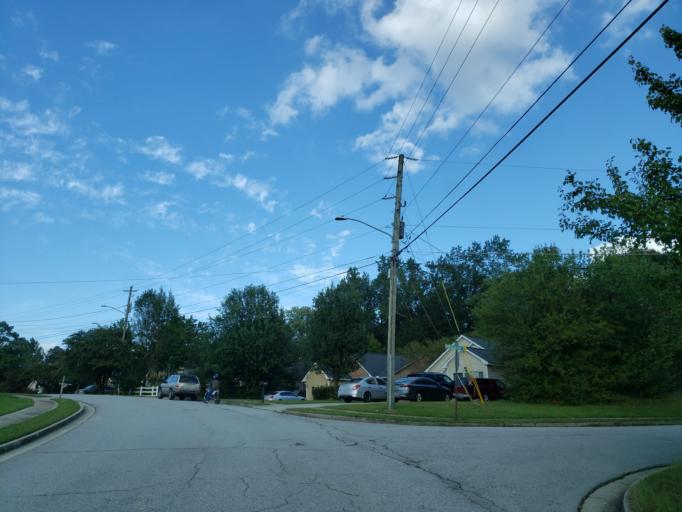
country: US
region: Georgia
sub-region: Douglas County
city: Douglasville
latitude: 33.7612
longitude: -84.7241
